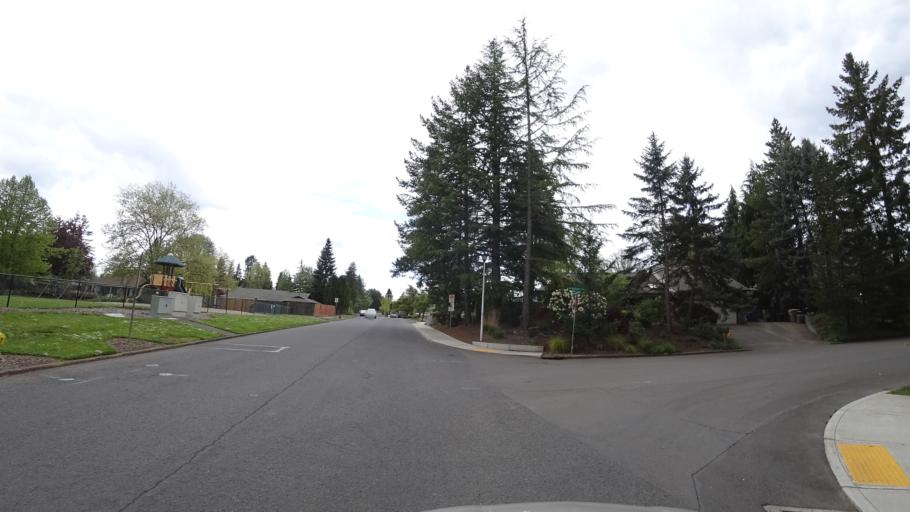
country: US
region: Oregon
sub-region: Washington County
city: Rockcreek
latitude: 45.5497
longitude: -122.8843
